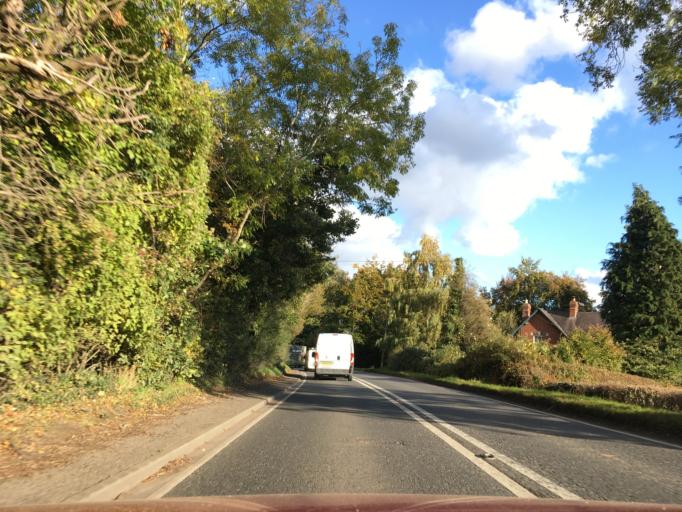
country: GB
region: England
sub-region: Herefordshire
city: Credenhill
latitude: 52.0719
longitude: -2.7941
